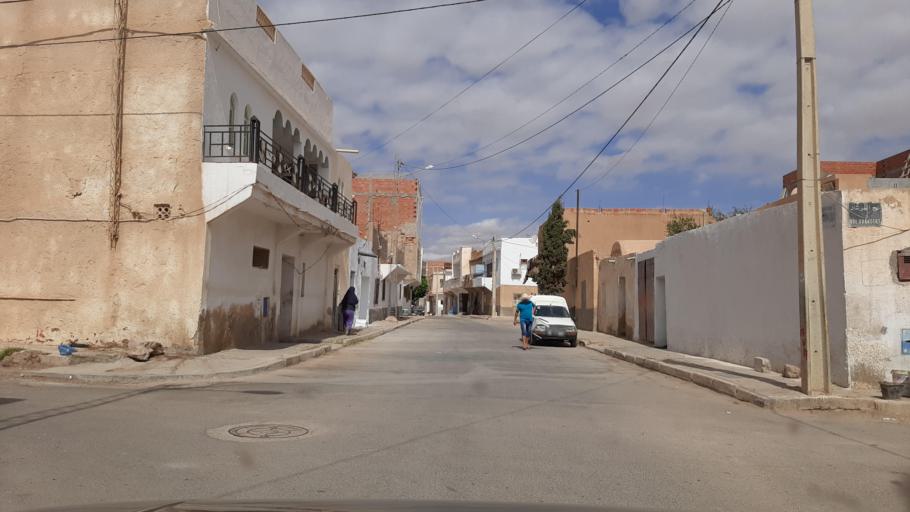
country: TN
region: Tataouine
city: Tataouine
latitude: 32.9291
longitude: 10.4553
